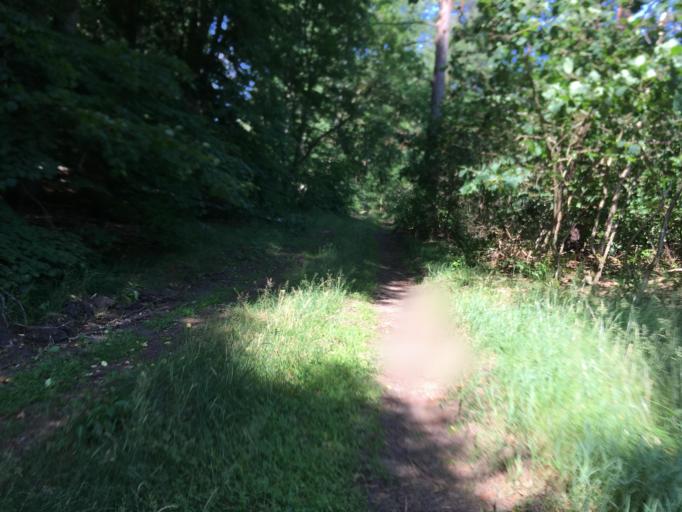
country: DE
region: Brandenburg
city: Marienwerder
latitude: 52.9216
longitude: 13.6591
